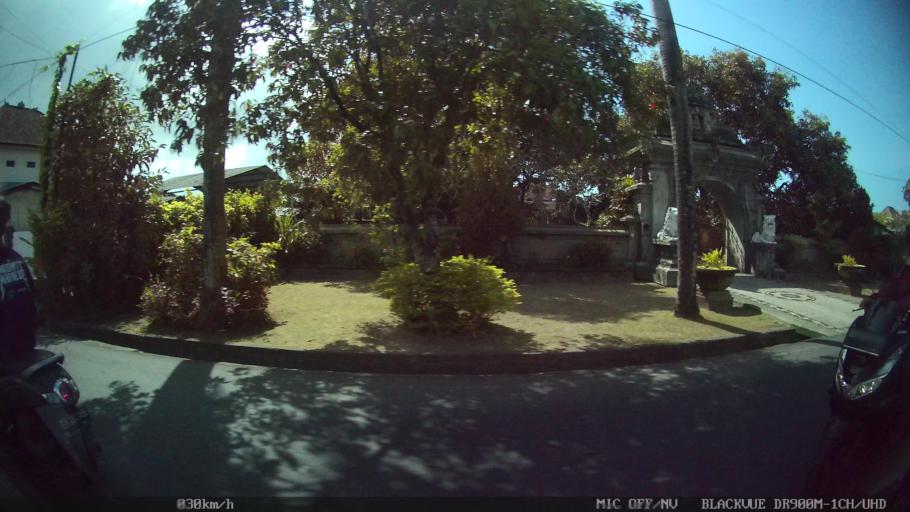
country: ID
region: Bali
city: Karyadharma
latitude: -8.7042
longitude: 115.1978
